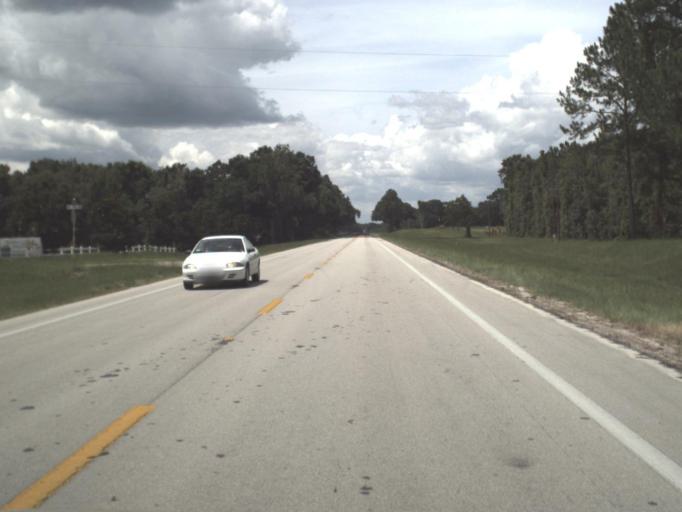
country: US
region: Florida
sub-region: Alachua County
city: High Springs
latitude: 29.7865
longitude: -82.6080
